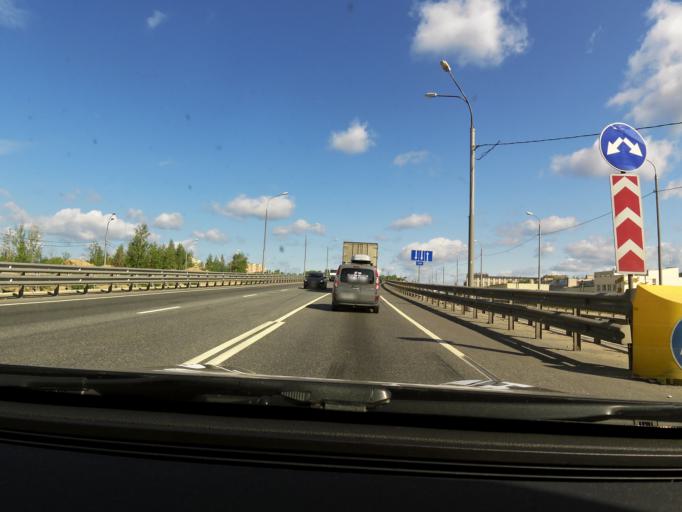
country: RU
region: Tverskaya
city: Tver
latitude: 56.8394
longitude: 35.7940
